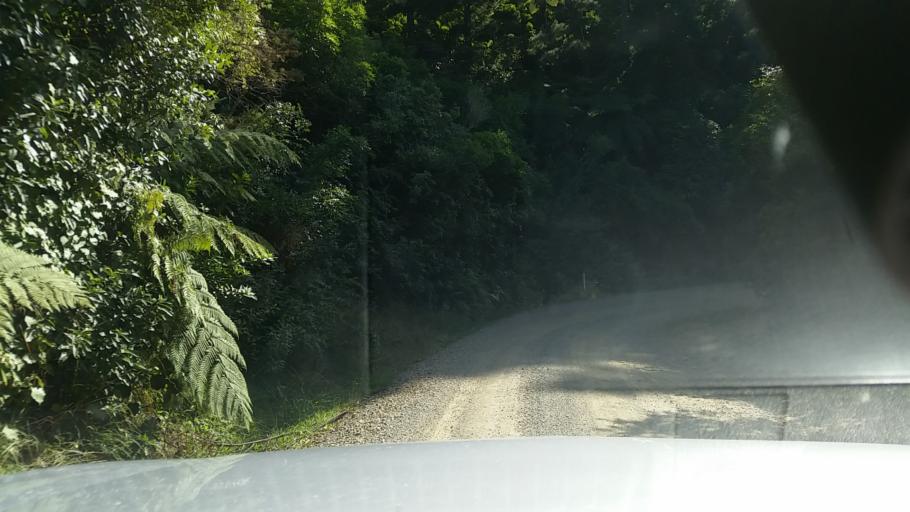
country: NZ
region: Marlborough
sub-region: Marlborough District
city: Picton
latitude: -41.2888
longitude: 174.1713
